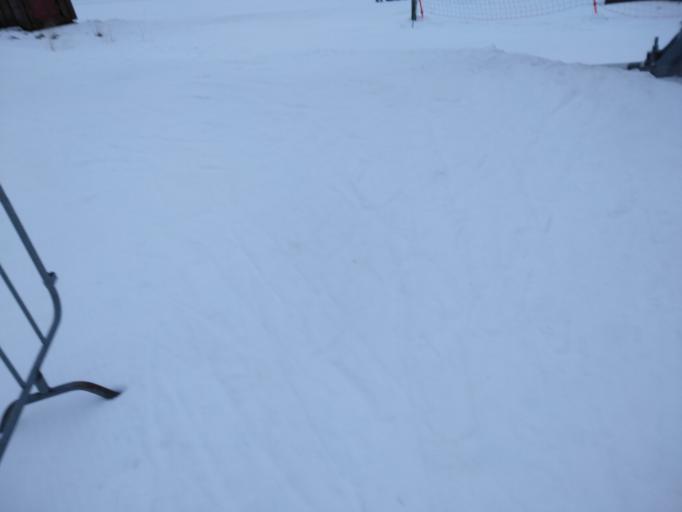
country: NO
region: Vest-Agder
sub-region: Sirdal
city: Tonstad
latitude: 59.0220
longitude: 6.9225
